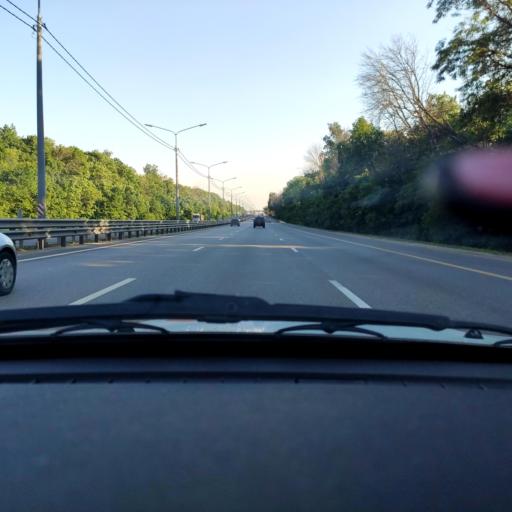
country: RU
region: Voronezj
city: Podgornoye
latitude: 51.8139
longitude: 39.2063
